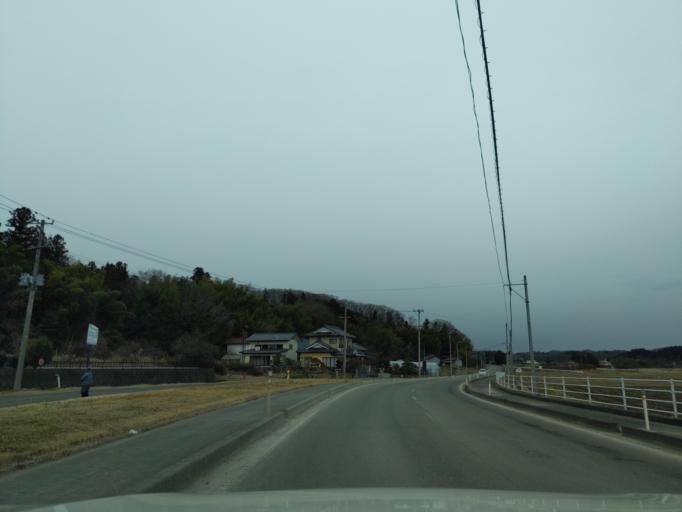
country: JP
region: Fukushima
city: Koriyama
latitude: 37.4363
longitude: 140.4144
